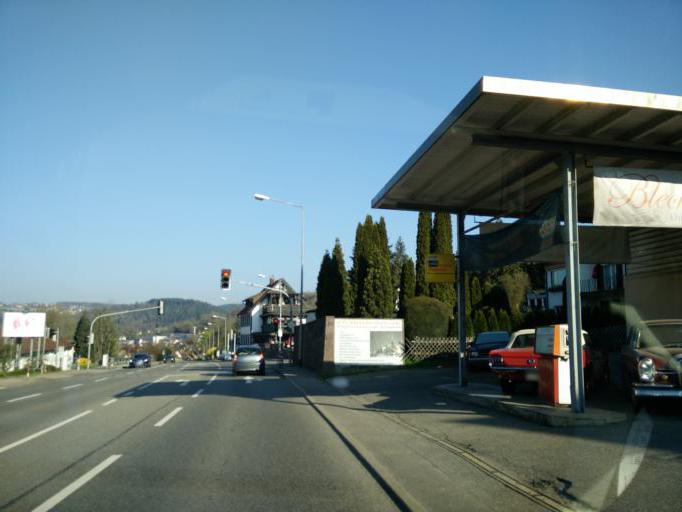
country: DE
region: Baden-Wuerttemberg
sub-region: Karlsruhe Region
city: Calw
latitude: 48.7102
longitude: 8.7584
